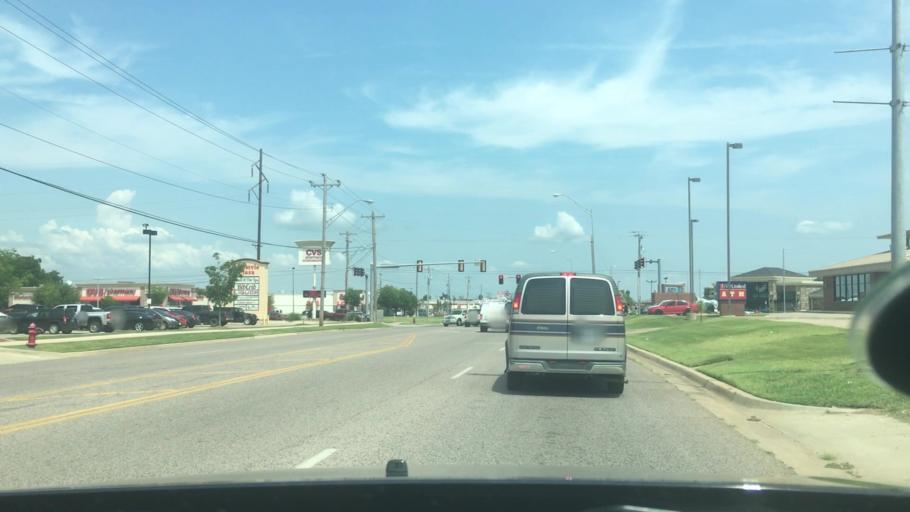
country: US
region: Oklahoma
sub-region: Pottawatomie County
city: Shawnee
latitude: 35.3753
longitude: -96.9297
